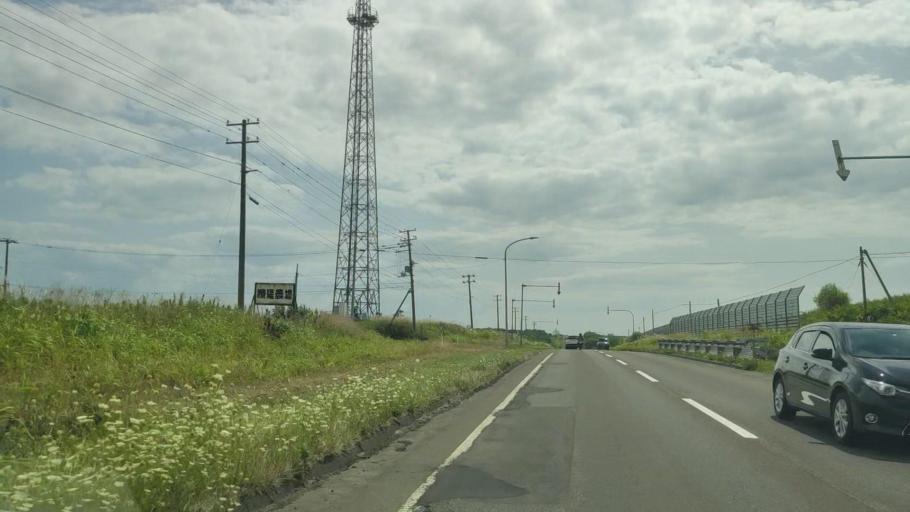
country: JP
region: Hokkaido
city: Rumoi
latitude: 44.4364
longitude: 141.7513
